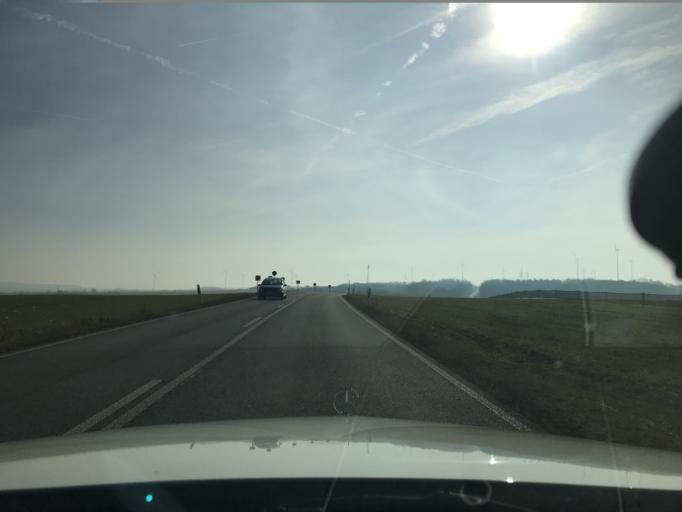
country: DE
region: Thuringia
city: Bad Langensalza
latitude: 51.0642
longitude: 10.6448
